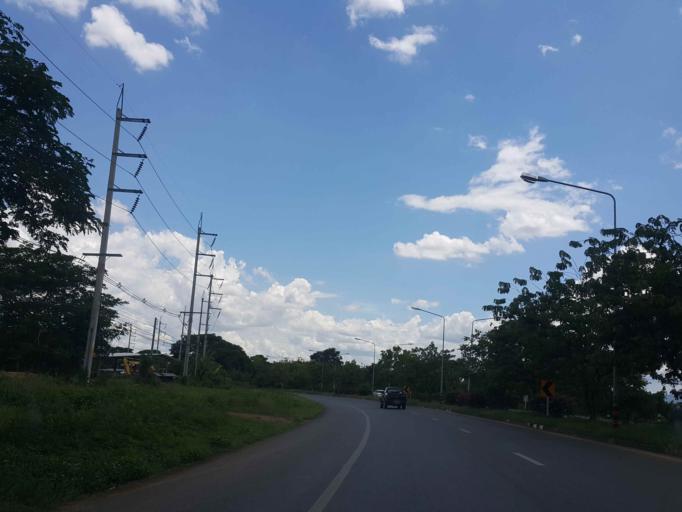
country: TH
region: Phrae
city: Nong Muang Khai
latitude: 18.2230
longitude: 100.1992
